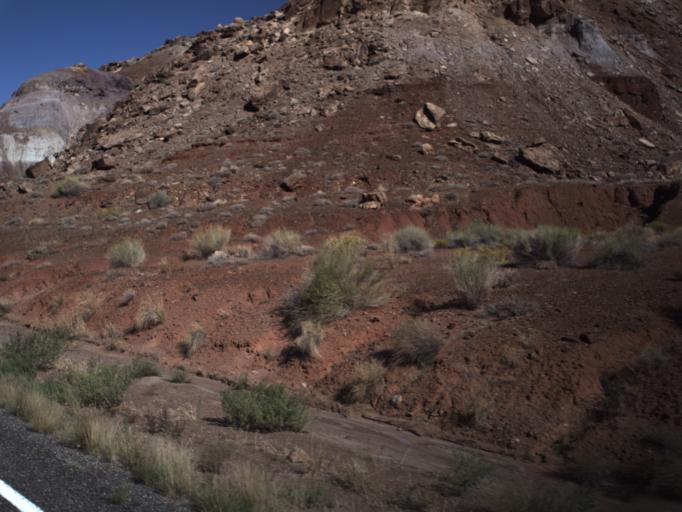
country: US
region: Utah
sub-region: San Juan County
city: Blanding
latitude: 37.9057
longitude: -110.4548
